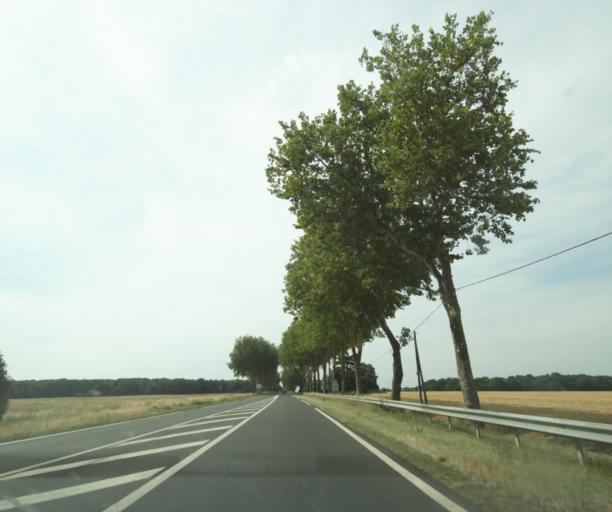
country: FR
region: Centre
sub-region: Departement d'Indre-et-Loire
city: Saint-Antoine-du-Rocher
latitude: 47.5018
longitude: 0.6005
